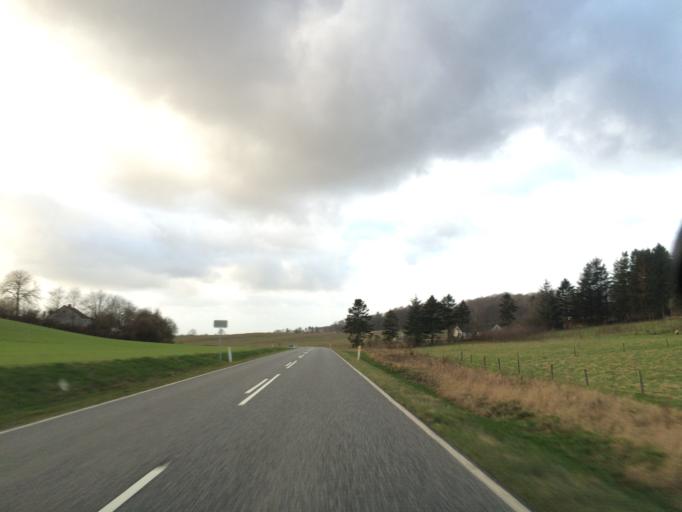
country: DK
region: Central Jutland
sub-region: Silkeborg Kommune
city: Svejbaek
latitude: 56.0989
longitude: 9.6382
